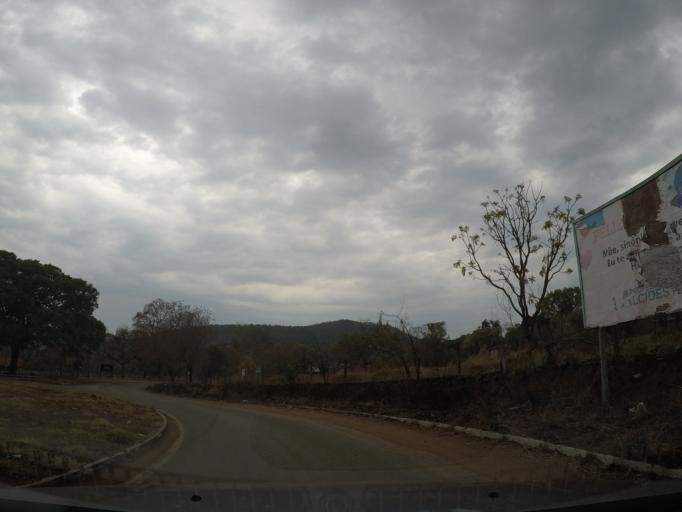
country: BR
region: Goias
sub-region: Pirenopolis
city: Pirenopolis
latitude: -15.8537
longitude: -48.9404
